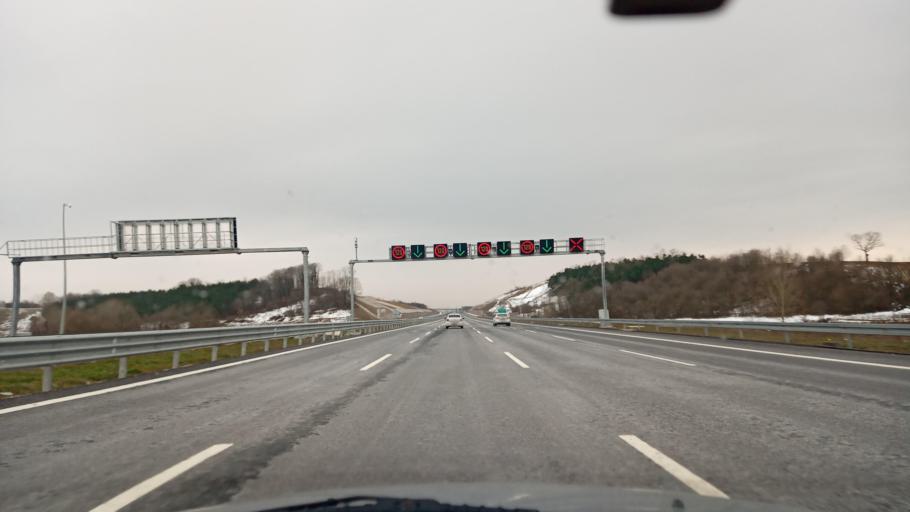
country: TR
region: Kocaeli
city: Akmese
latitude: 40.8464
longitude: 30.2490
